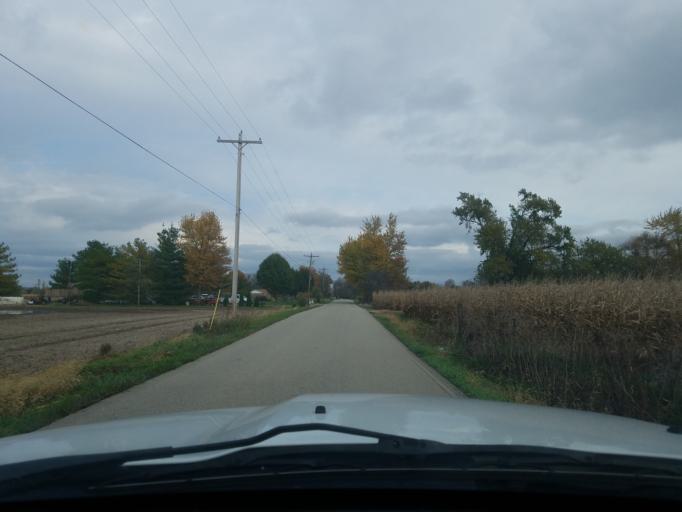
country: US
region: Indiana
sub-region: Shelby County
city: Shelbyville
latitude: 39.5546
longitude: -85.8048
